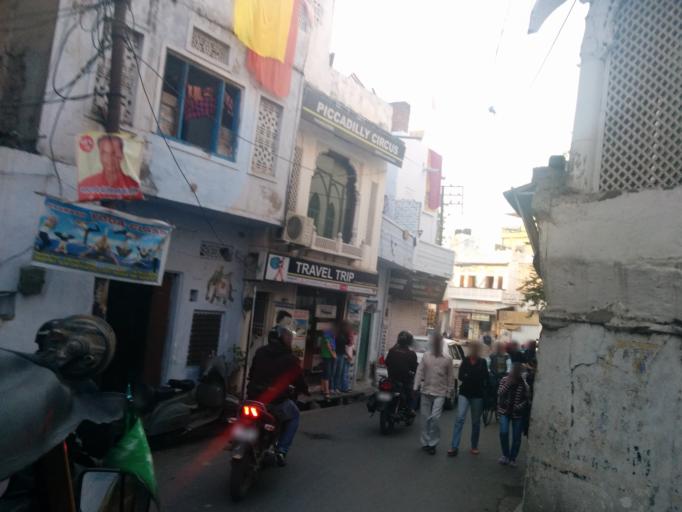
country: IN
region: Rajasthan
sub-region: Udaipur
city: Udaipur
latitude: 24.5809
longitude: 73.6822
